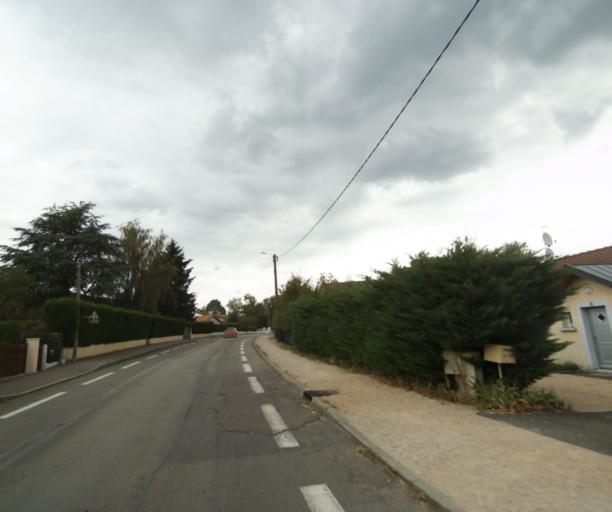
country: FR
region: Bourgogne
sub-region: Departement de Saone-et-Loire
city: Tournus
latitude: 46.5712
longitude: 4.9006
